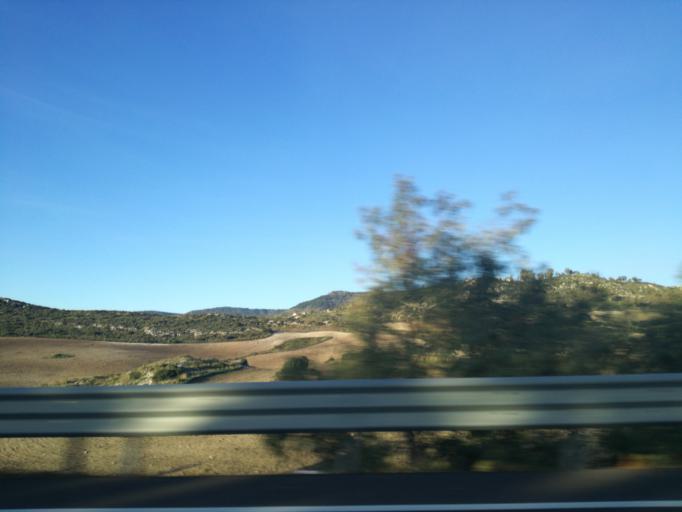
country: IT
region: Sicily
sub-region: Catania
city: San Michele di Ganzaria
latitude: 37.2161
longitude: 14.4156
